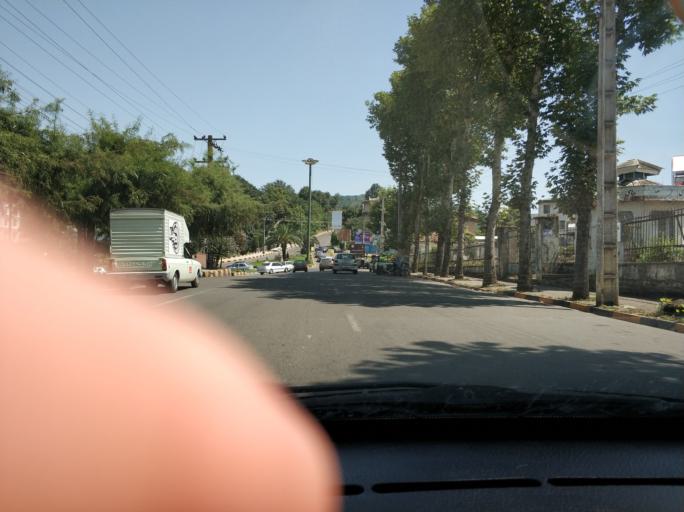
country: IR
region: Gilan
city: Lahijan
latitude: 37.1960
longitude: 50.0177
